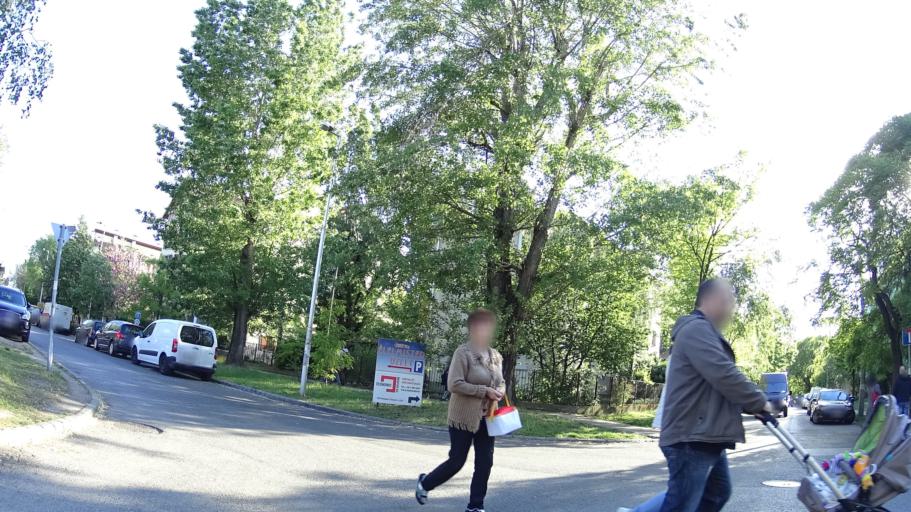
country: HU
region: Budapest
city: Budapest XX. keruelet
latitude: 47.4330
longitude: 19.0934
